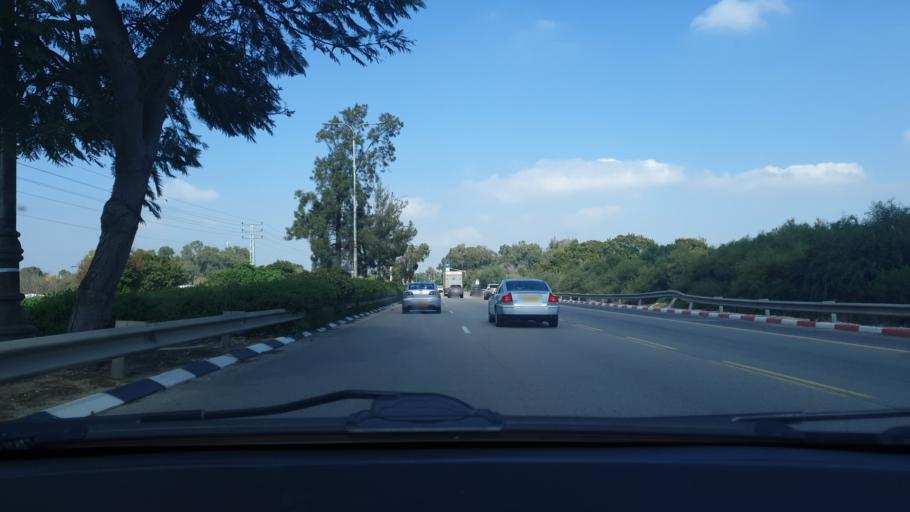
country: IL
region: Central District
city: Bet Dagan
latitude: 31.9871
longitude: 34.8115
